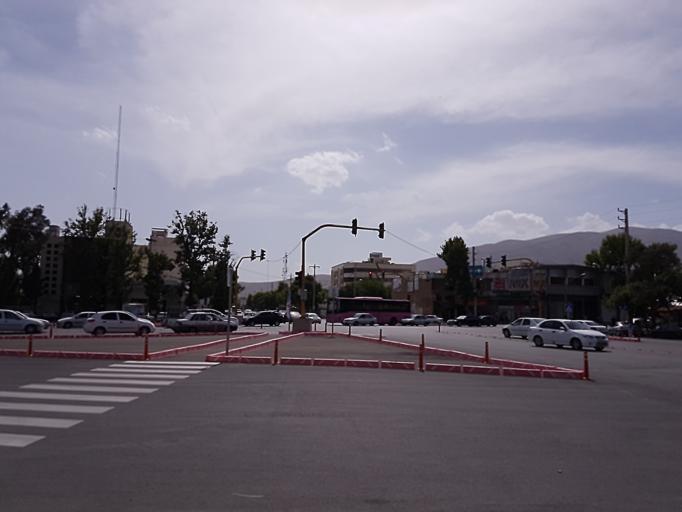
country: IR
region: Fars
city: Shiraz
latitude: 29.6541
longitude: 52.4853
